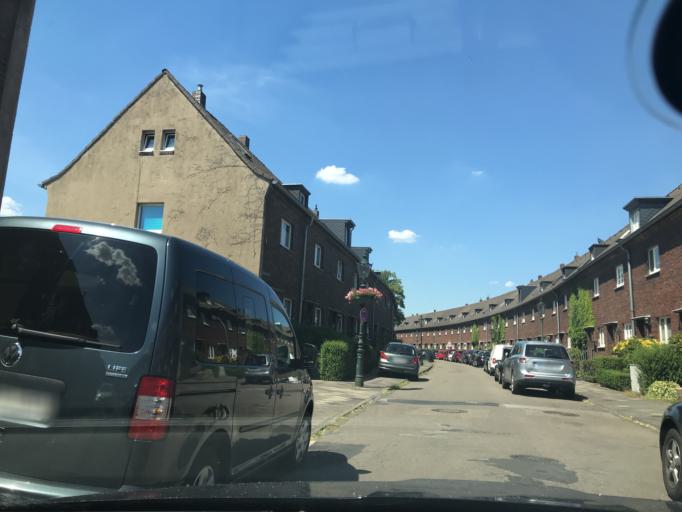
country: DE
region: North Rhine-Westphalia
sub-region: Regierungsbezirk Dusseldorf
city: Dusseldorf
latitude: 51.2680
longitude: 6.7972
